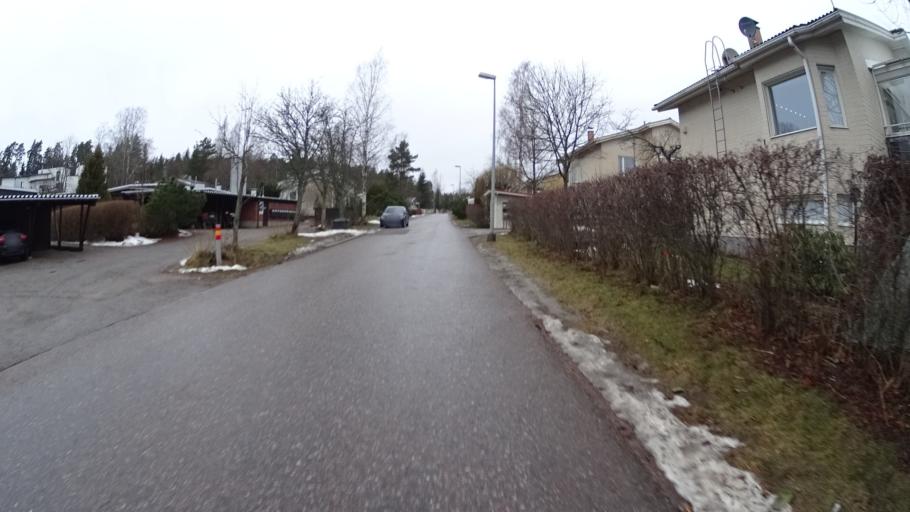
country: FI
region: Uusimaa
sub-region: Helsinki
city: Koukkuniemi
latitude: 60.1829
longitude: 24.7601
